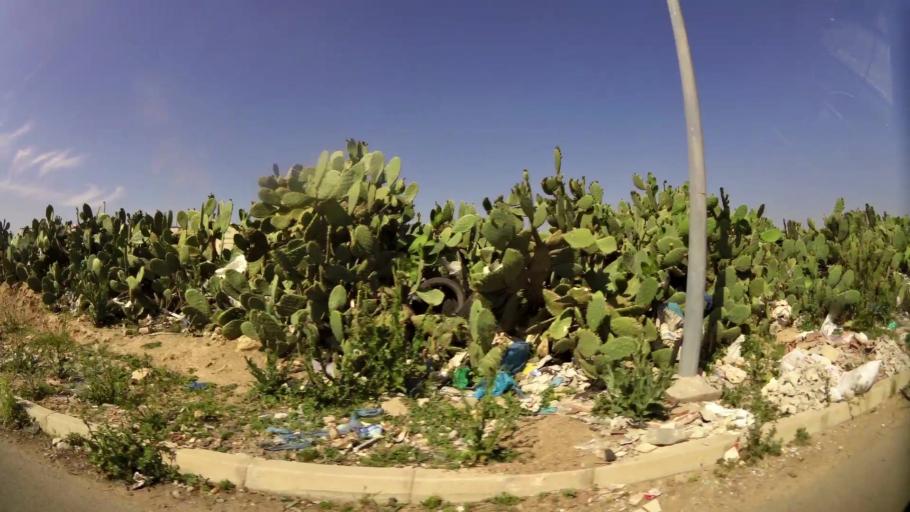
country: MA
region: Oriental
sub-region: Oujda-Angad
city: Oujda
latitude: 34.6974
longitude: -1.8761
